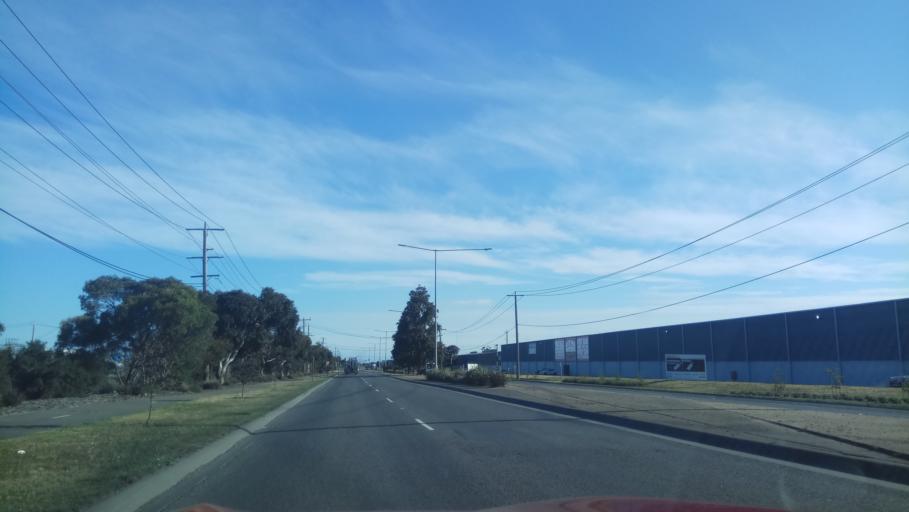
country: AU
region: Victoria
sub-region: Hobsons Bay
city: Altona North
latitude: -37.8344
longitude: 144.8264
